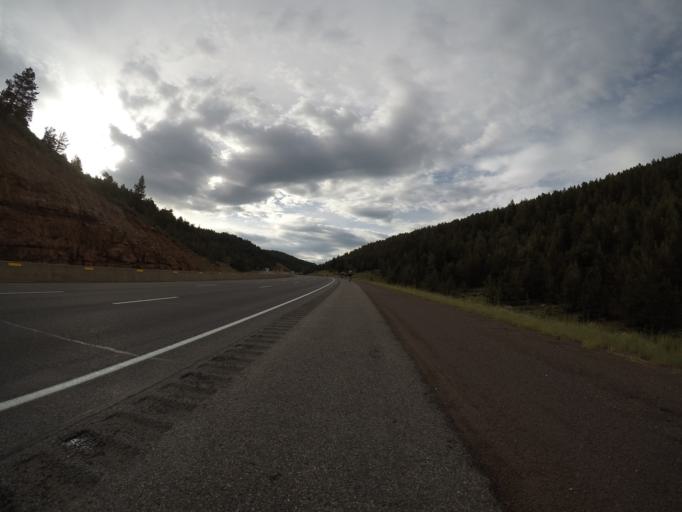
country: US
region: Wyoming
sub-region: Albany County
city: Laramie
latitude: 41.2631
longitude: -105.4641
